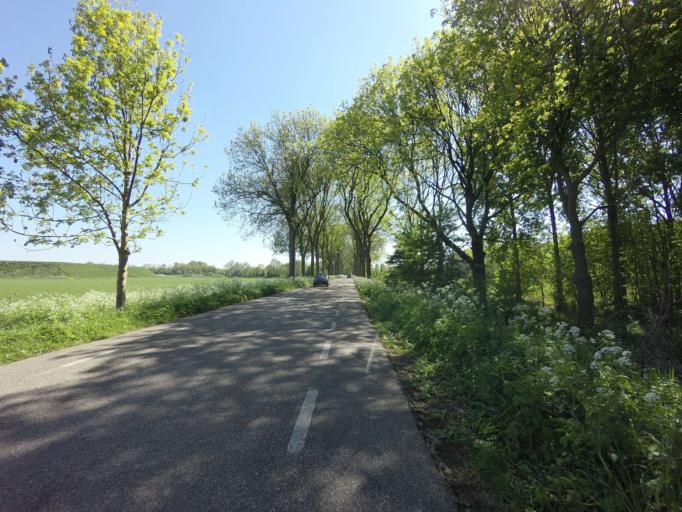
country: NL
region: North Brabant
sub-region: Gemeente Moerdijk
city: Klundert
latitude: 51.6644
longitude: 4.6095
